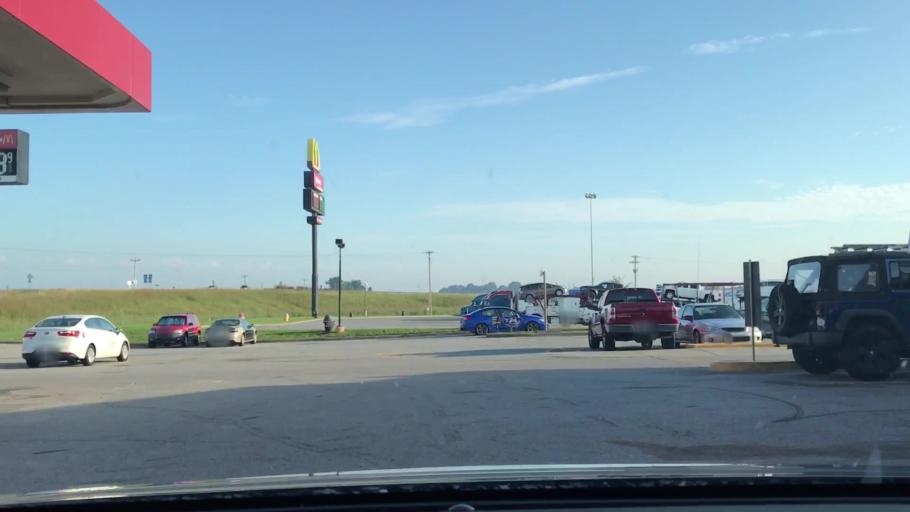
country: US
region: Kentucky
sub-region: Christian County
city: Oak Grove
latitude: 36.6784
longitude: -87.4051
